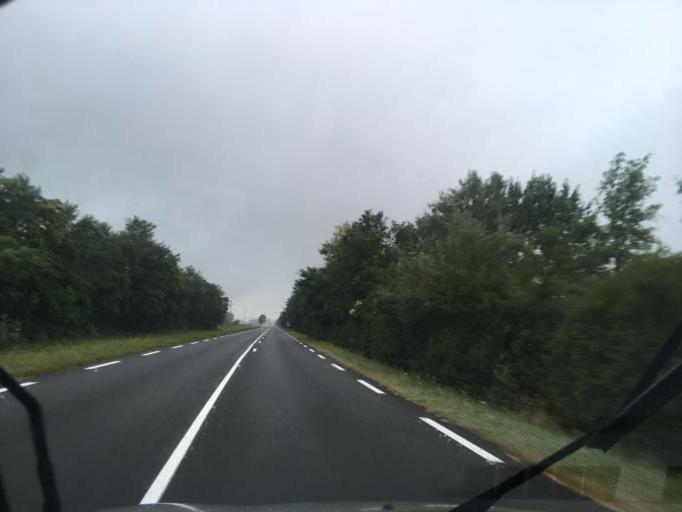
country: FR
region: Midi-Pyrenees
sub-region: Departement des Hautes-Pyrenees
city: Andrest
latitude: 43.3253
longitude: 0.0693
